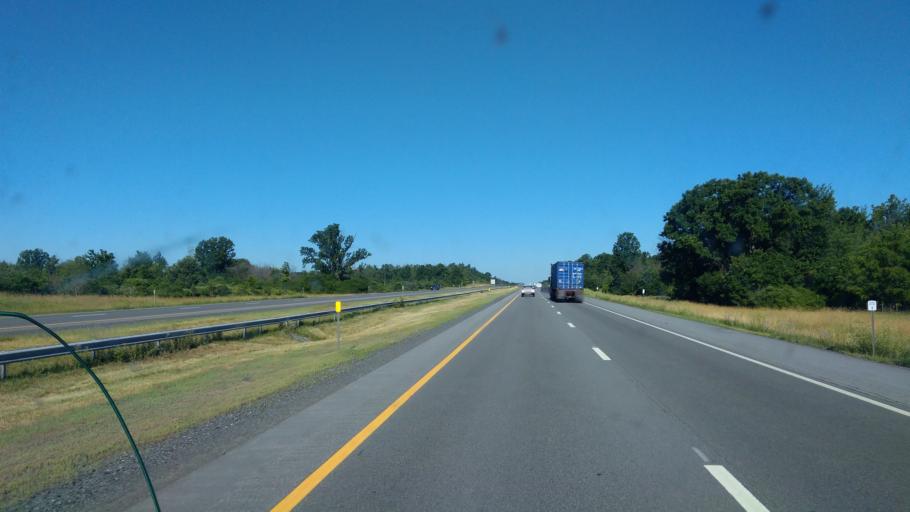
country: US
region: New York
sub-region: Livingston County
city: Caledonia
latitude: 43.0299
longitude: -77.8507
